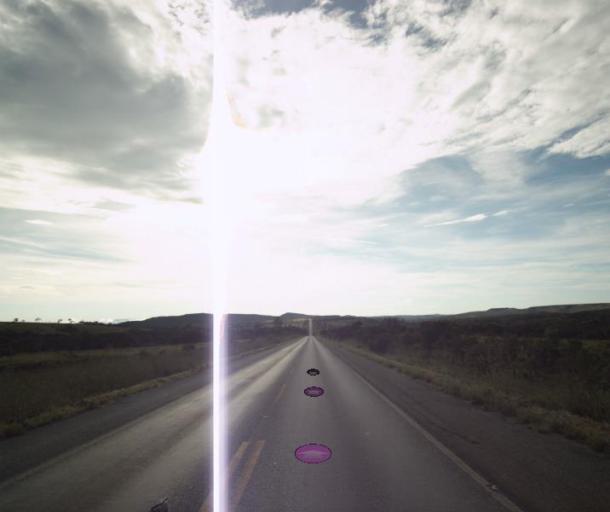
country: BR
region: Goias
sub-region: Pirenopolis
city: Pirenopolis
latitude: -15.7511
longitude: -48.6383
